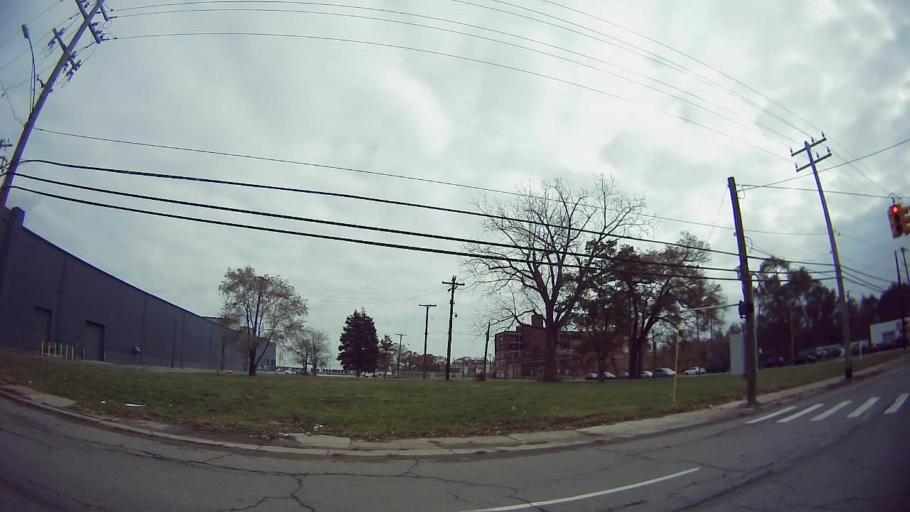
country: US
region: Michigan
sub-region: Wayne County
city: Hamtramck
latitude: 42.3908
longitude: -83.0374
